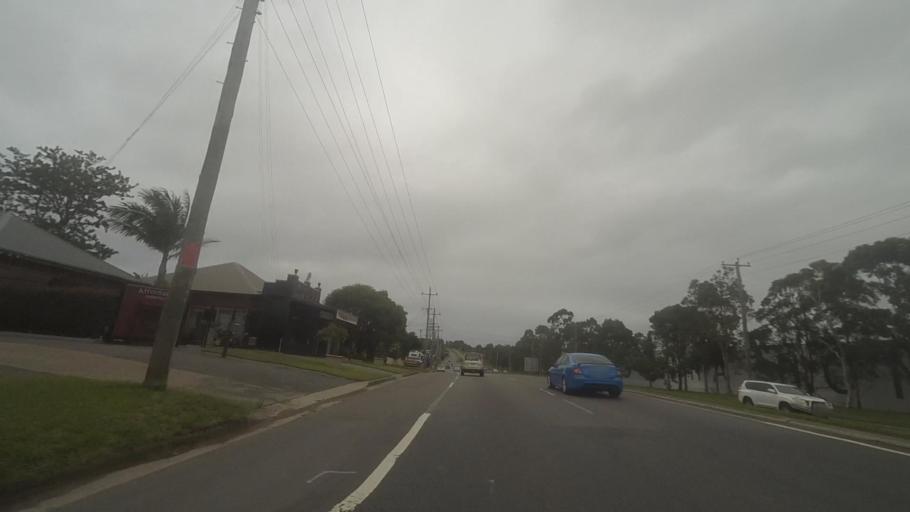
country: AU
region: New South Wales
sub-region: Newcastle
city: Mayfield West
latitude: -32.8715
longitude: 151.7106
